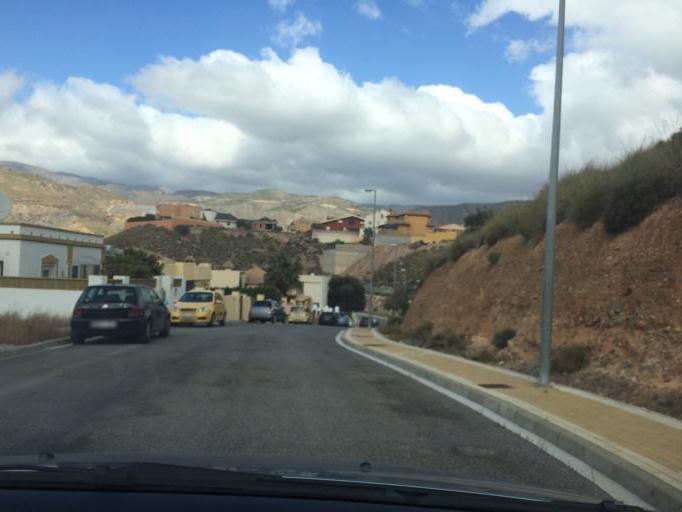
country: ES
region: Andalusia
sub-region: Provincia de Almeria
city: Vicar
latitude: 36.8312
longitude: -2.6125
